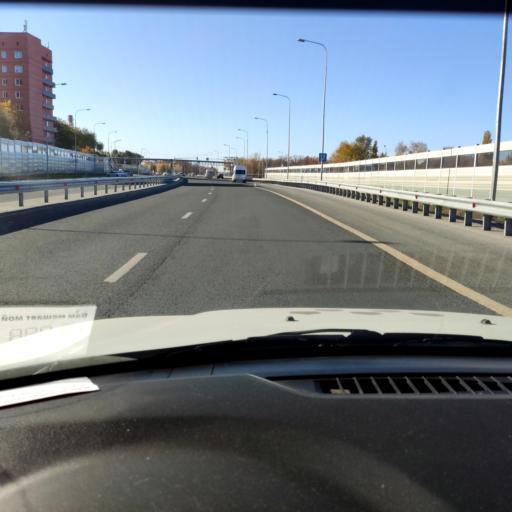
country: RU
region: Samara
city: Bereza
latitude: 53.5129
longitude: 50.1469
